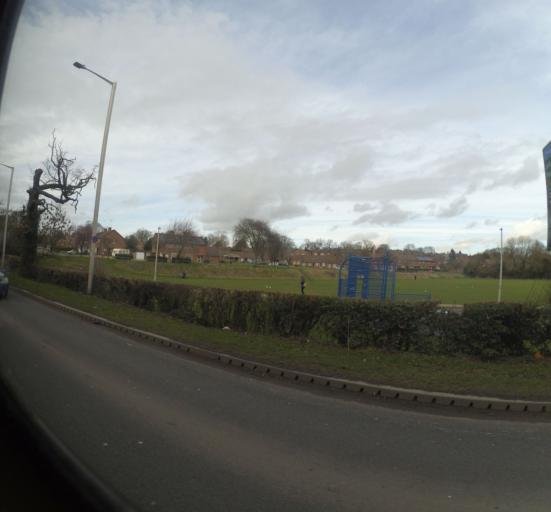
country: GB
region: England
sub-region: Warwickshire
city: Rugby
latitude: 52.3834
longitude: -1.2701
